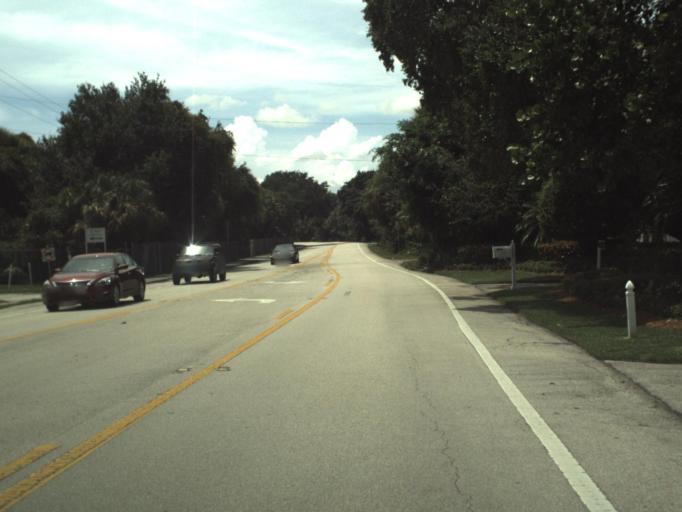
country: US
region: Florida
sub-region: Palm Beach County
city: North Palm Beach
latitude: 26.8362
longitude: -80.0489
